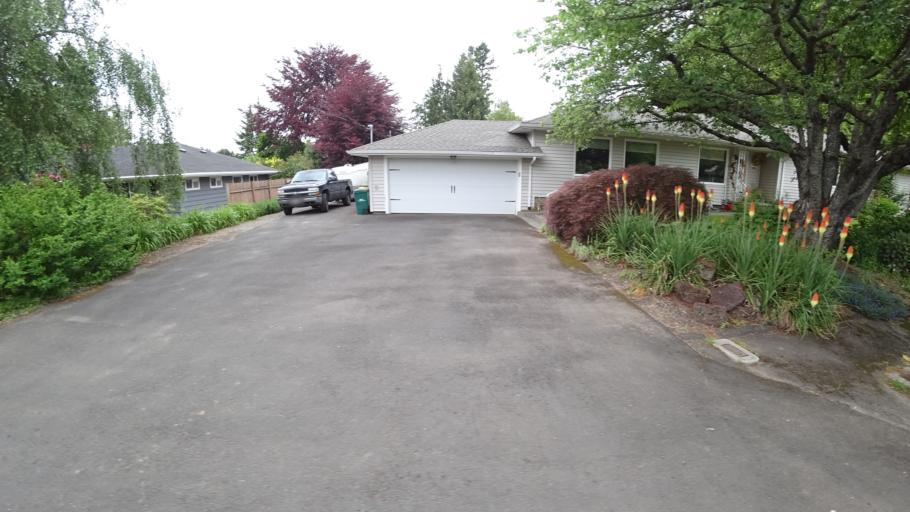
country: US
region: Oregon
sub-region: Washington County
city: Garden Home-Whitford
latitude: 45.4743
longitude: -122.7468
